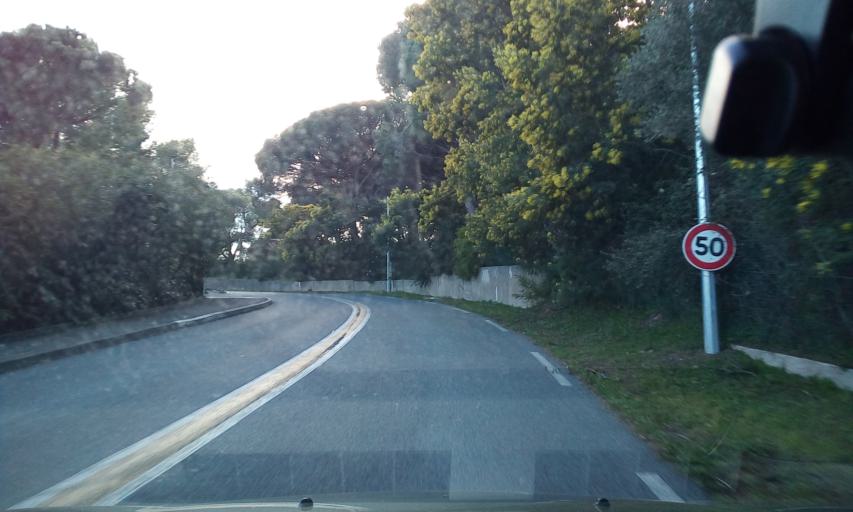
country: FR
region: Provence-Alpes-Cote d'Azur
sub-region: Departement du Var
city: Saint-Raphael
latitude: 43.4394
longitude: 6.7671
